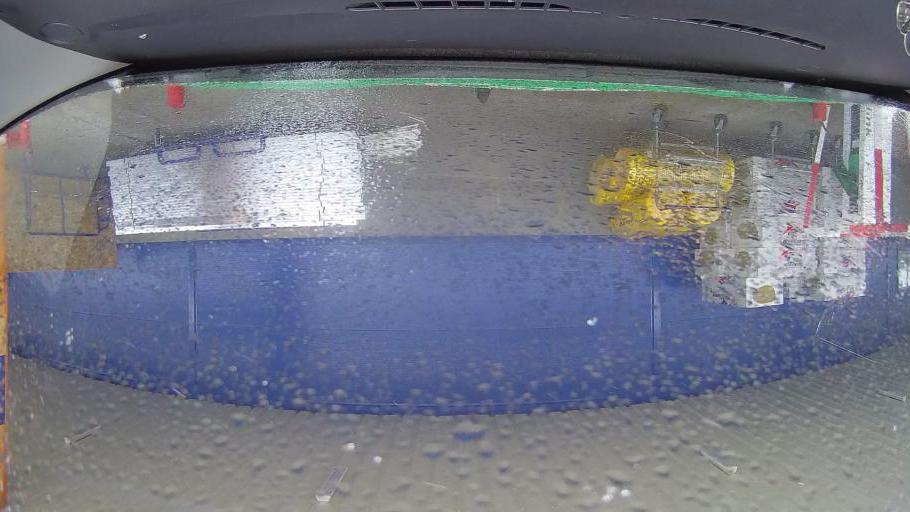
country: RO
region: Hunedoara
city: Hunedoara
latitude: 45.7667
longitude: 22.9032
